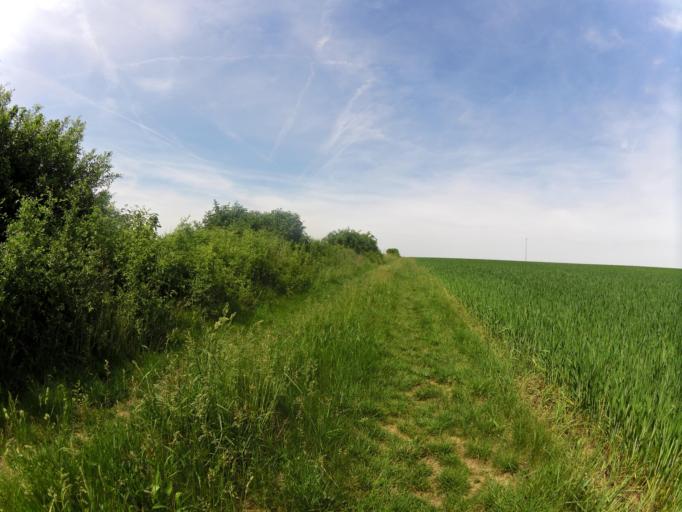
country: DE
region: Bavaria
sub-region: Regierungsbezirk Unterfranken
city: Ochsenfurt
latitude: 49.6651
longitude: 10.0304
